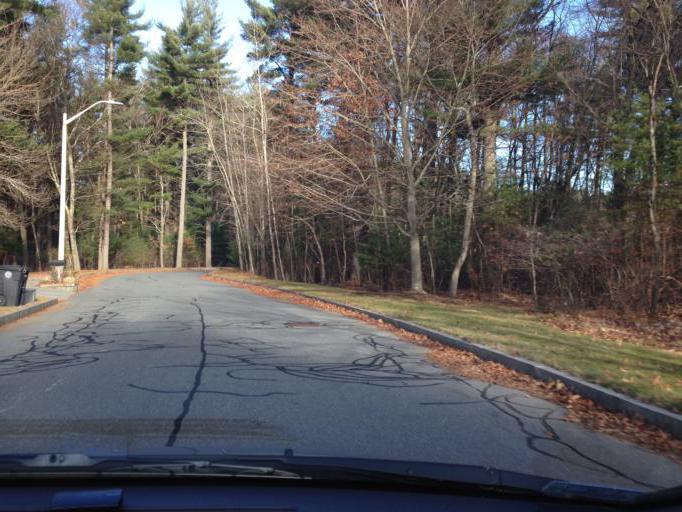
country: US
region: Massachusetts
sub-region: Middlesex County
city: Bedford
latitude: 42.4991
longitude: -71.3023
